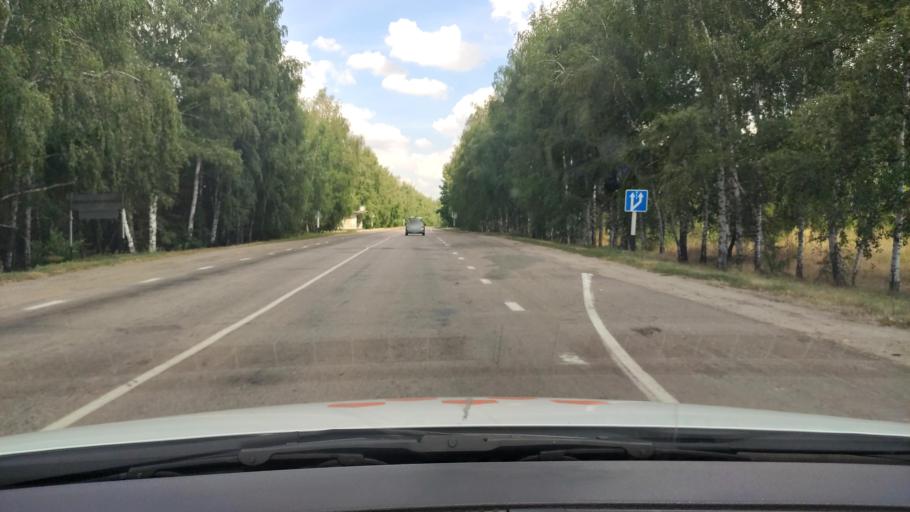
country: RU
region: Voronezj
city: Sadovoye
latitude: 51.7805
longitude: 40.5401
